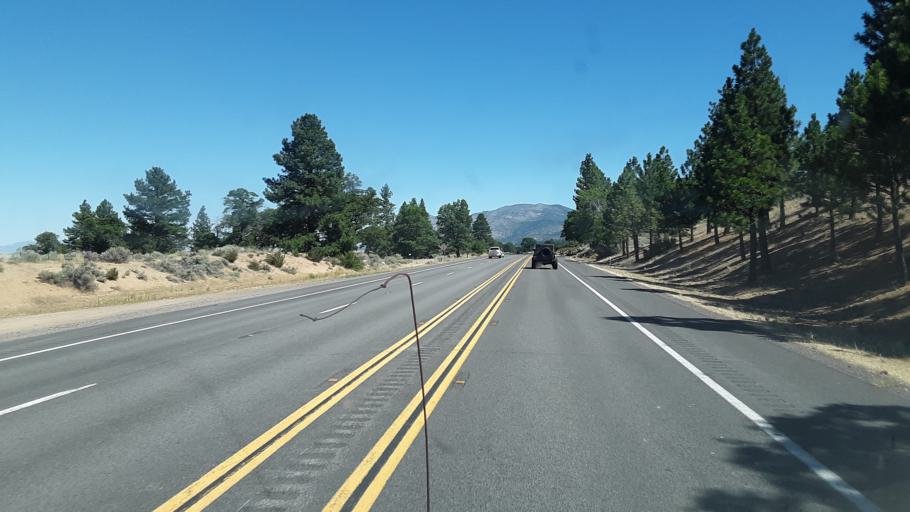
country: US
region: California
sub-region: Lassen County
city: Janesville
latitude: 40.2190
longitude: -120.4302
